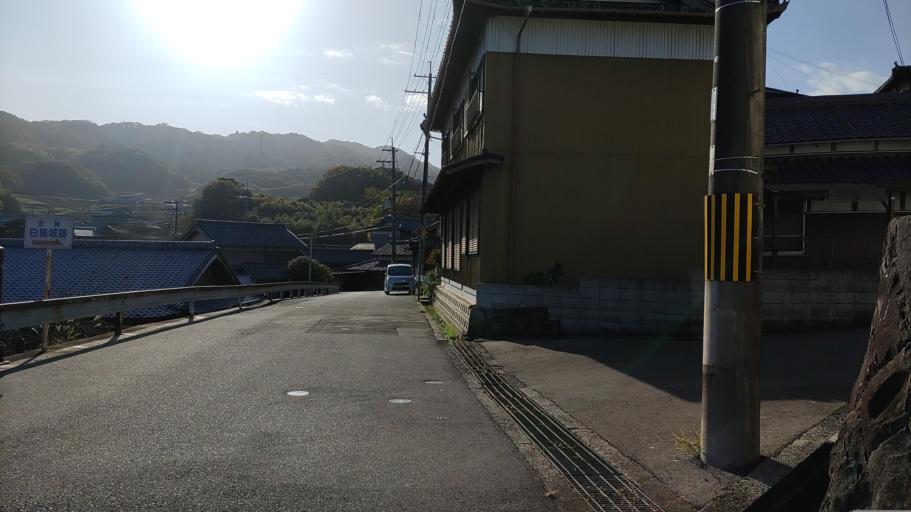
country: JP
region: Hyogo
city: Sumoto
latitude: 34.3894
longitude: 134.8174
